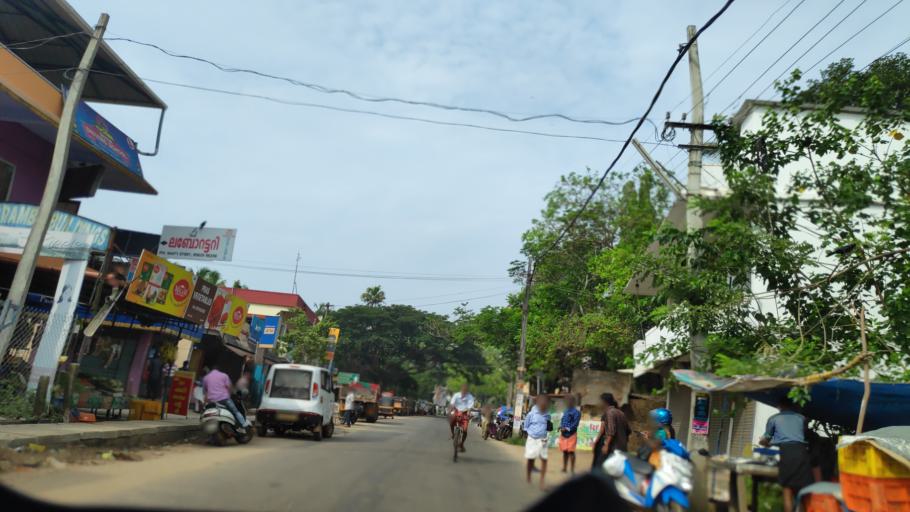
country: IN
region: Kerala
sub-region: Alappuzha
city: Kutiatodu
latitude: 9.7946
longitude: 76.3558
